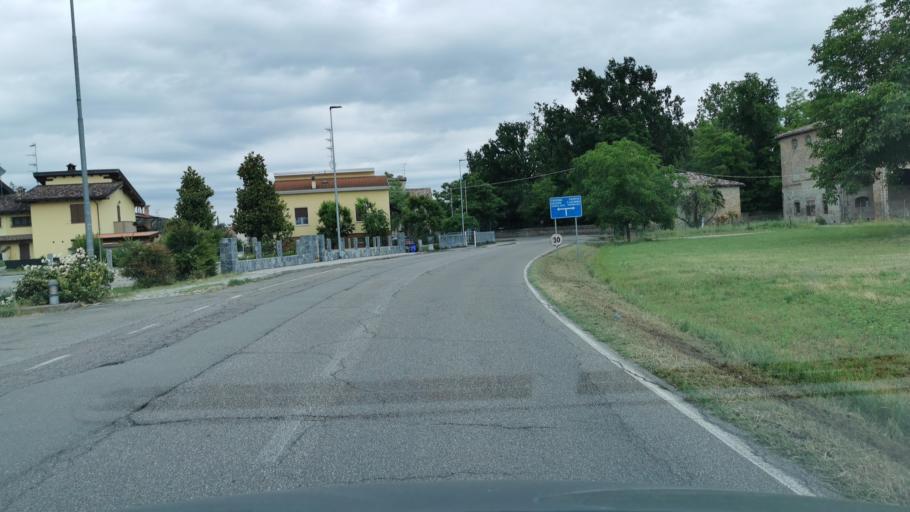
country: IT
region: Emilia-Romagna
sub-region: Provincia di Parma
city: Soragna
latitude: 44.9270
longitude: 10.1185
